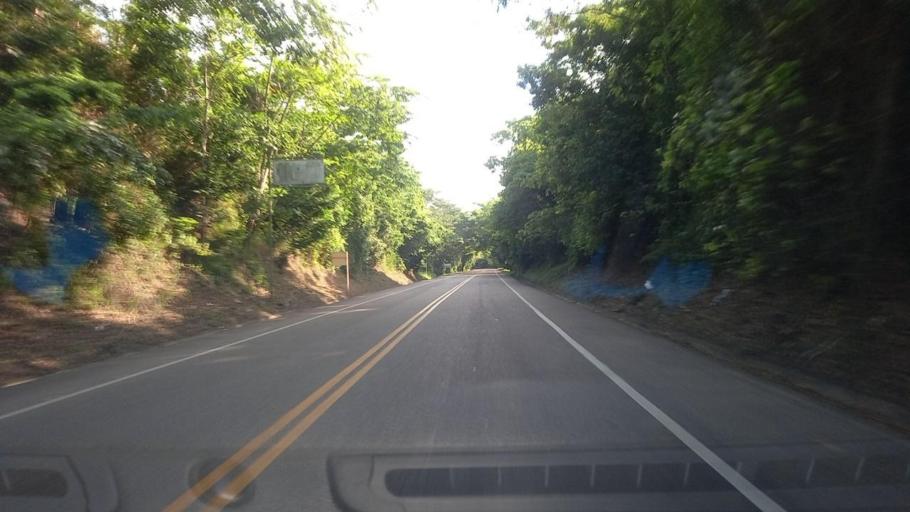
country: CO
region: Antioquia
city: Puerto Triunfo
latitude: 5.8895
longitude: -74.5709
